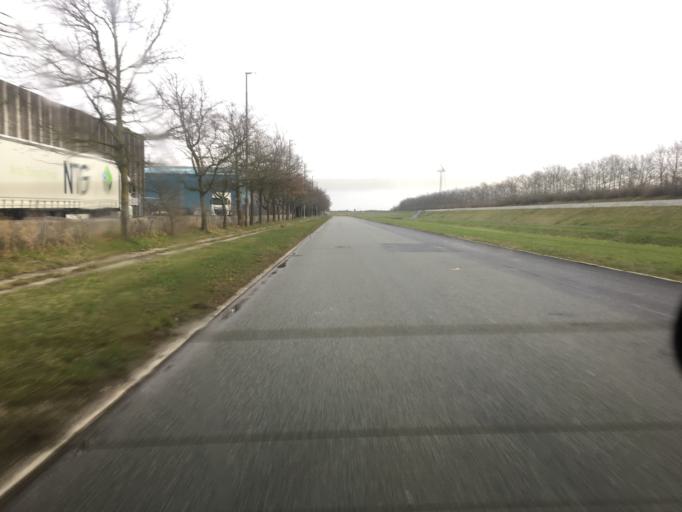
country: DK
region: Capital Region
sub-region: Hvidovre Kommune
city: Hvidovre
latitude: 55.6049
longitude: 12.4848
